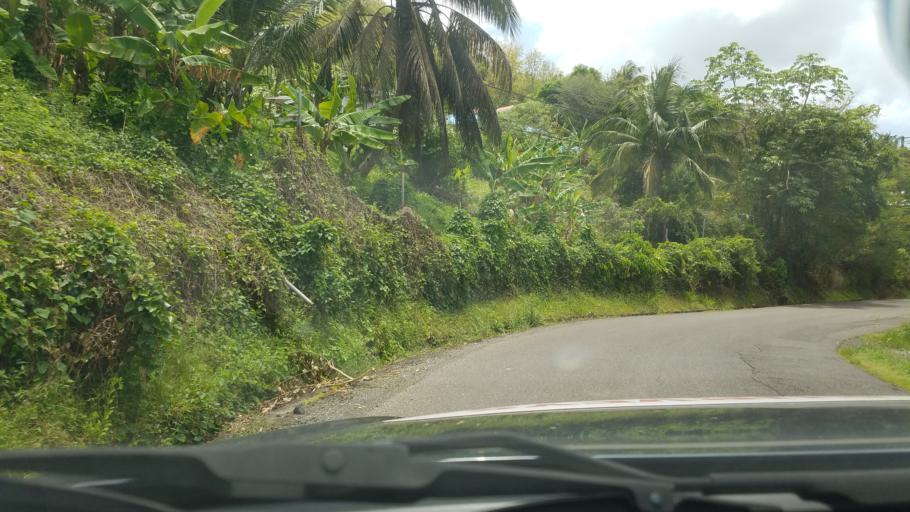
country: LC
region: Gros-Islet
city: Gros Islet
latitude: 14.0579
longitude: -60.9396
